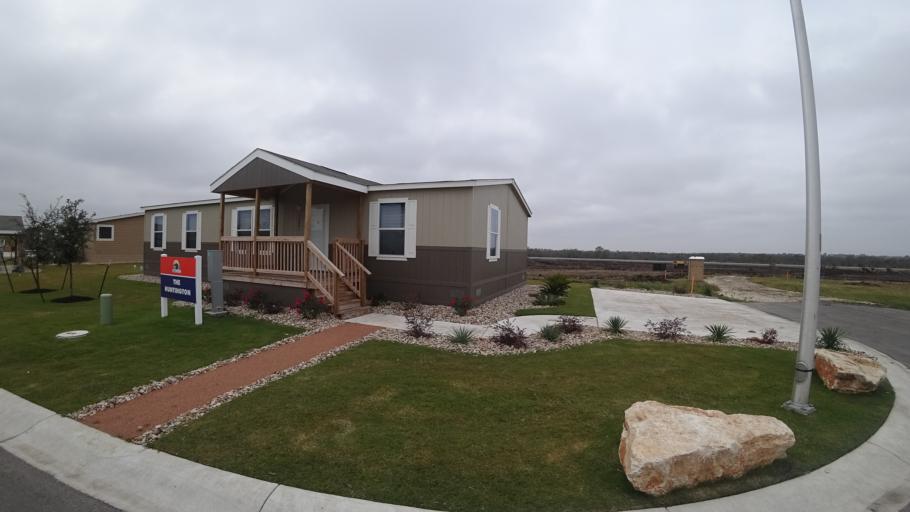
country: US
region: Texas
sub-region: Travis County
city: Pflugerville
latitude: 30.4078
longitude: -97.6069
